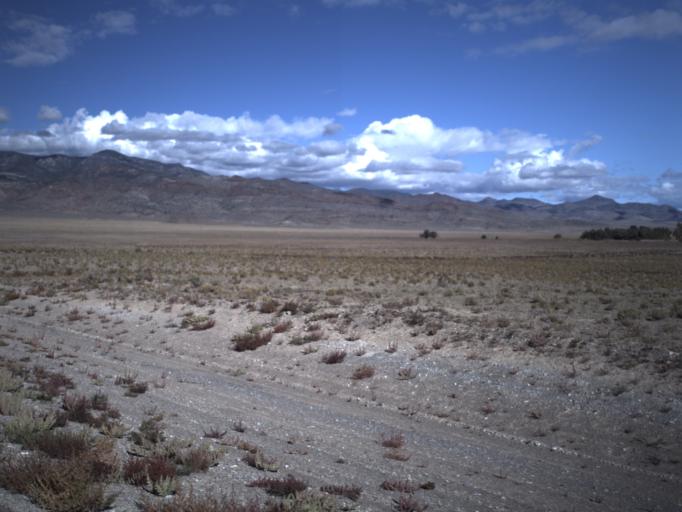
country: US
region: Utah
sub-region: Beaver County
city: Milford
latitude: 38.4785
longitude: -113.4314
